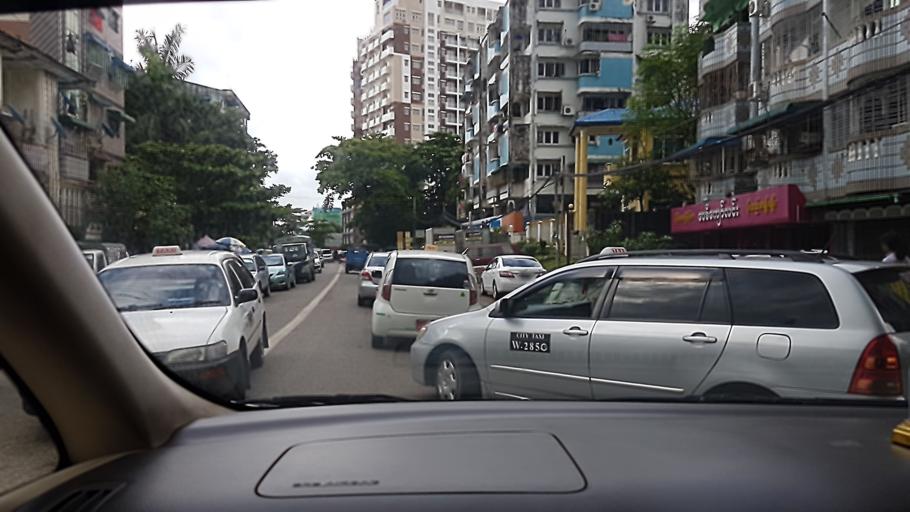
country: MM
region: Yangon
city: Yangon
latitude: 16.8014
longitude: 96.1301
